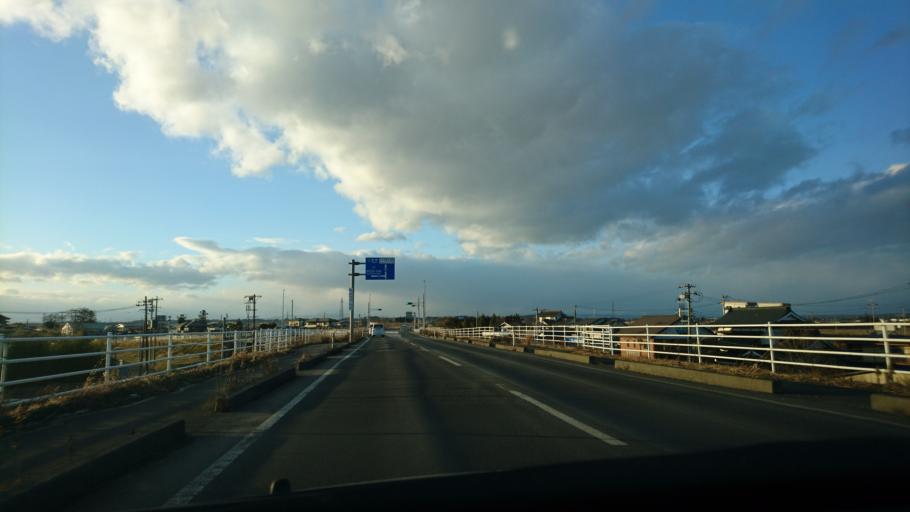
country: JP
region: Miyagi
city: Wakuya
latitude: 38.7223
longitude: 141.1524
